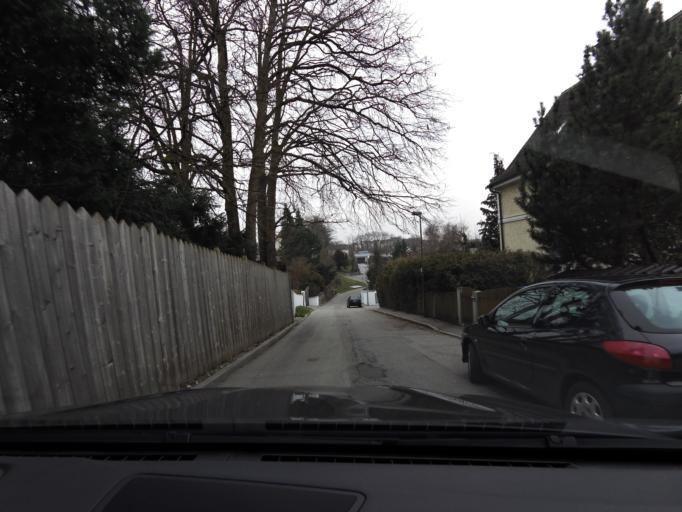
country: DE
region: Bavaria
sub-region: Lower Bavaria
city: Landshut
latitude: 48.5264
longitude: 12.1558
